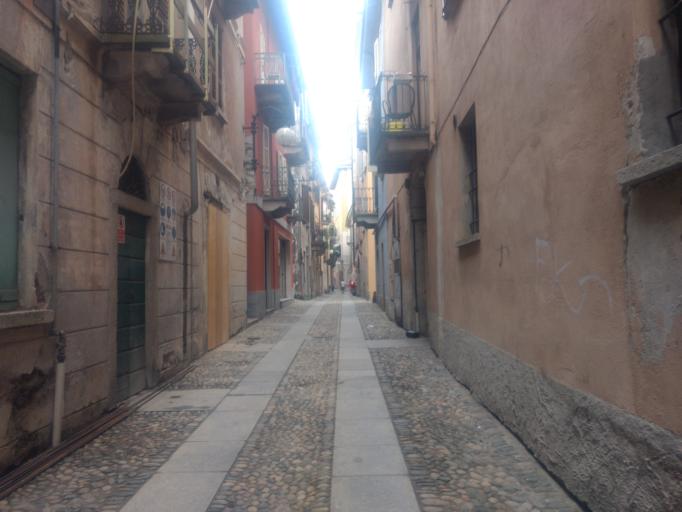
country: IT
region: Piedmont
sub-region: Provincia Verbano-Cusio-Ossola
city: Verbania
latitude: 45.9226
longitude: 8.5487
